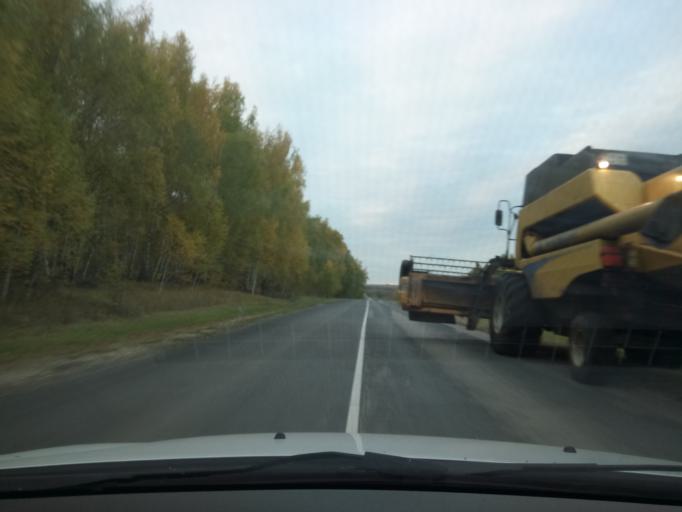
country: RU
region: Nizjnij Novgorod
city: Bol'shoye Murashkino
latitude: 55.7311
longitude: 44.7754
